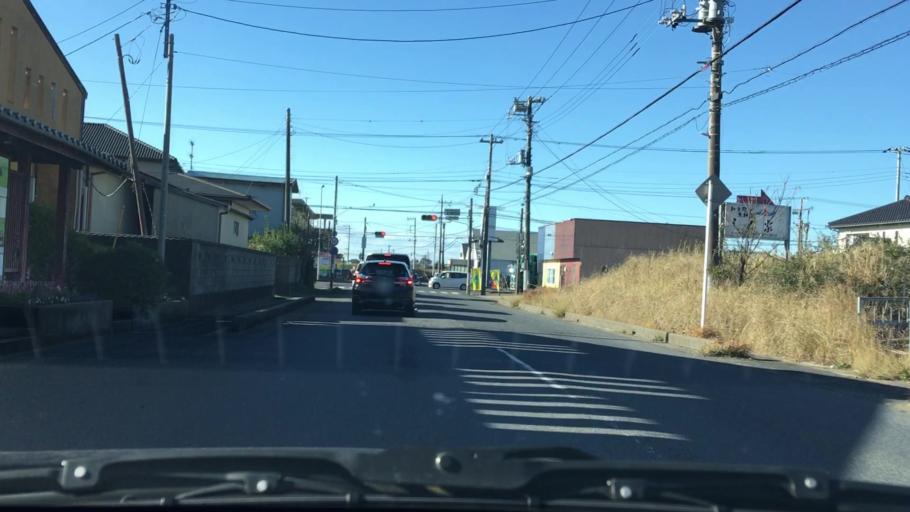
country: JP
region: Chiba
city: Omigawa
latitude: 35.8603
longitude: 140.7006
